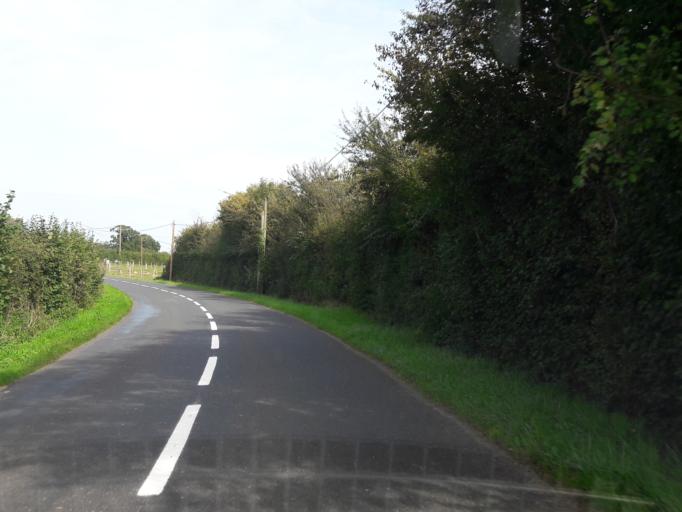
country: FR
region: Lower Normandy
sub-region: Departement du Calvados
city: Bayeux
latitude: 49.2034
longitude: -0.7201
